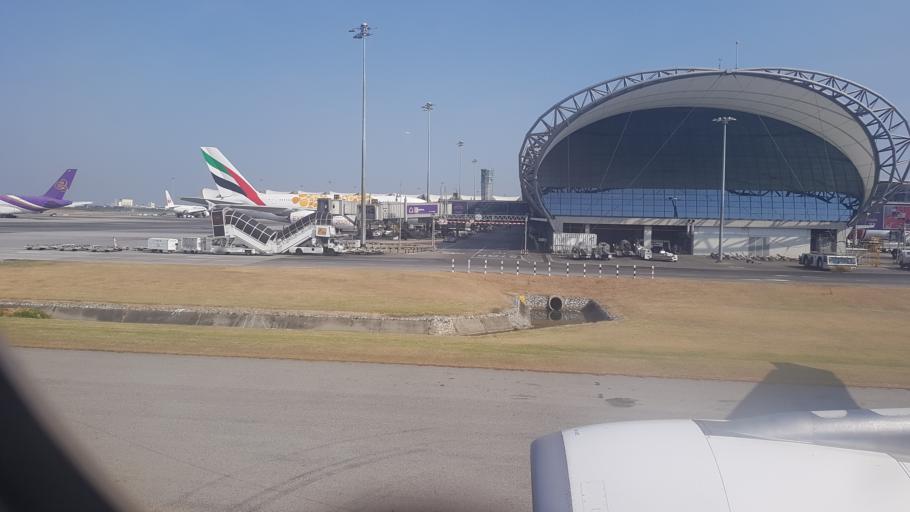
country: TH
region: Bangkok
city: Lat Krabang
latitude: 13.6873
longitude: 100.7453
